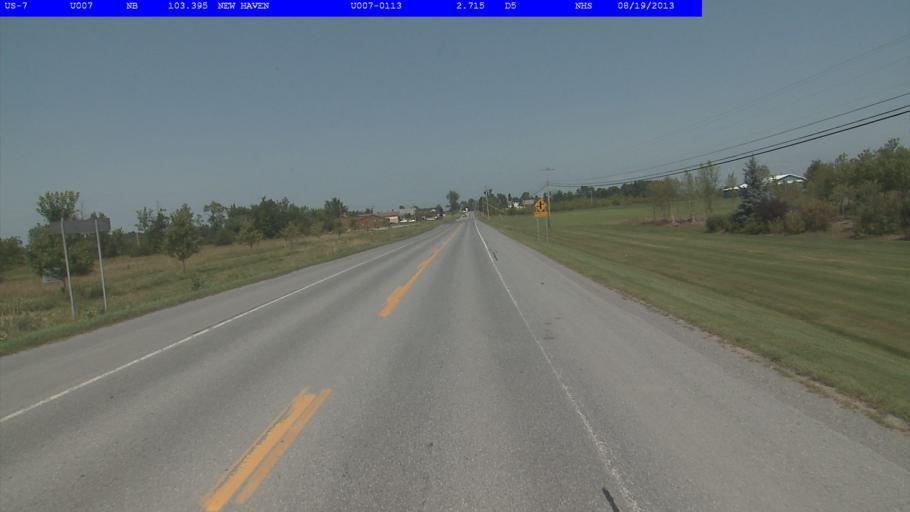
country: US
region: Vermont
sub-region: Addison County
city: Middlebury (village)
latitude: 44.0847
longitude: -73.1762
